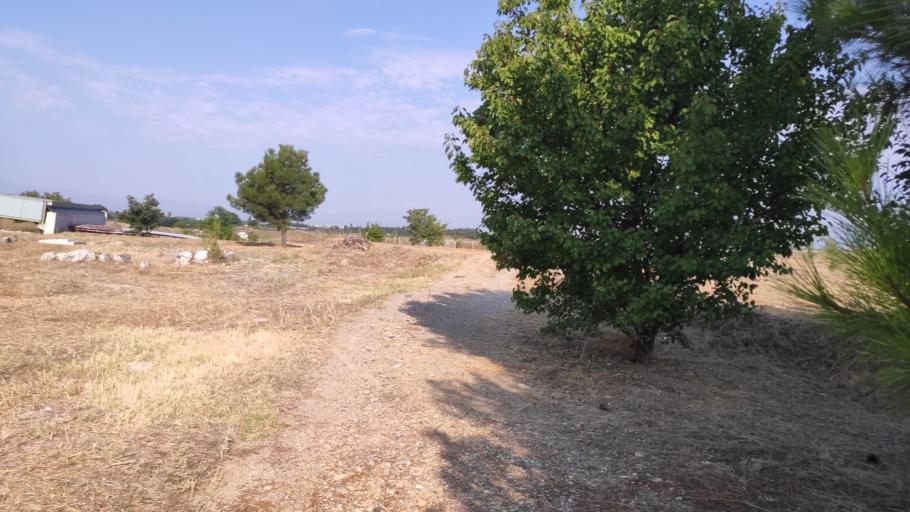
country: GR
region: Central Macedonia
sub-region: Nomos Pellis
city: Pella
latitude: 40.7553
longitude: 22.5184
